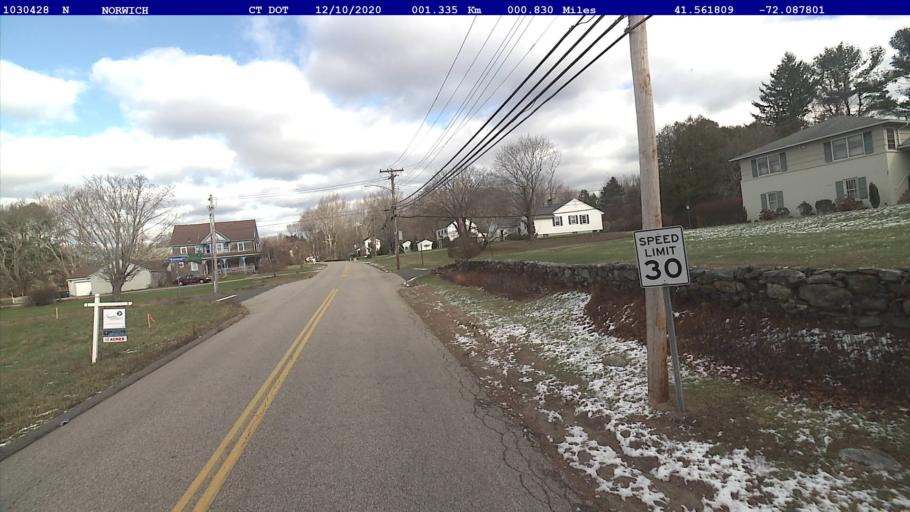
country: US
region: Connecticut
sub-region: New London County
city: Norwich
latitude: 41.5618
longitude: -72.0878
